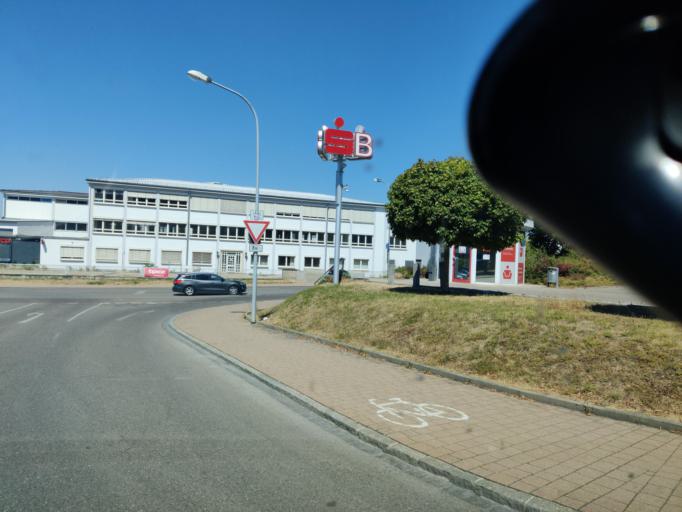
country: DE
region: Bavaria
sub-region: Regierungsbezirk Mittelfranken
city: Weissenburg in Bayern
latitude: 49.0206
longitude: 10.9651
